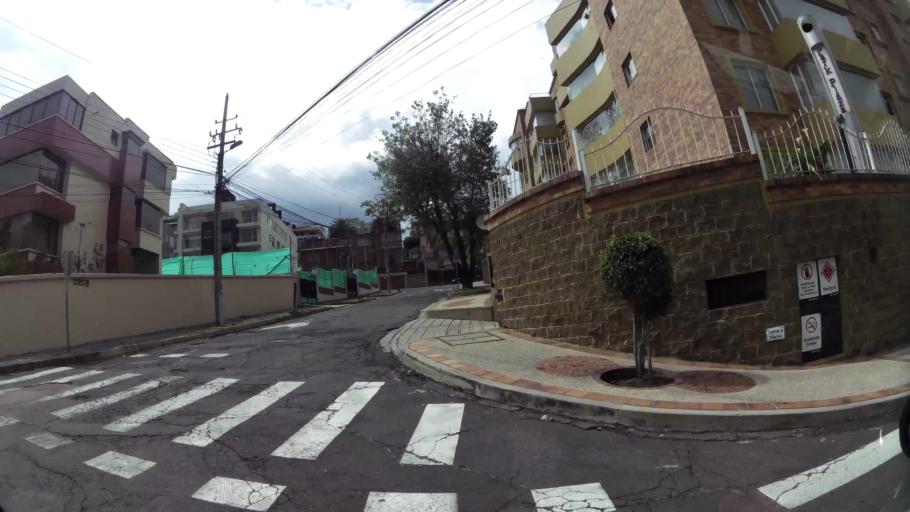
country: EC
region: Pichincha
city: Quito
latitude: -0.1685
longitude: -78.4933
